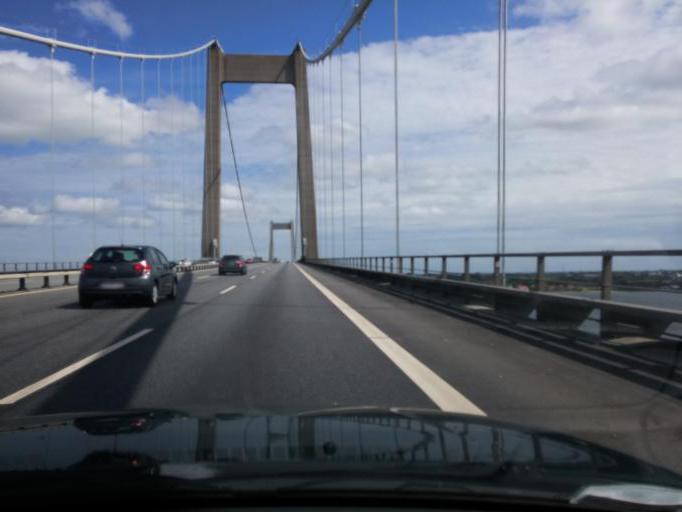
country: DK
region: South Denmark
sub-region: Middelfart Kommune
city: Middelfart
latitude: 55.5199
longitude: 9.7418
